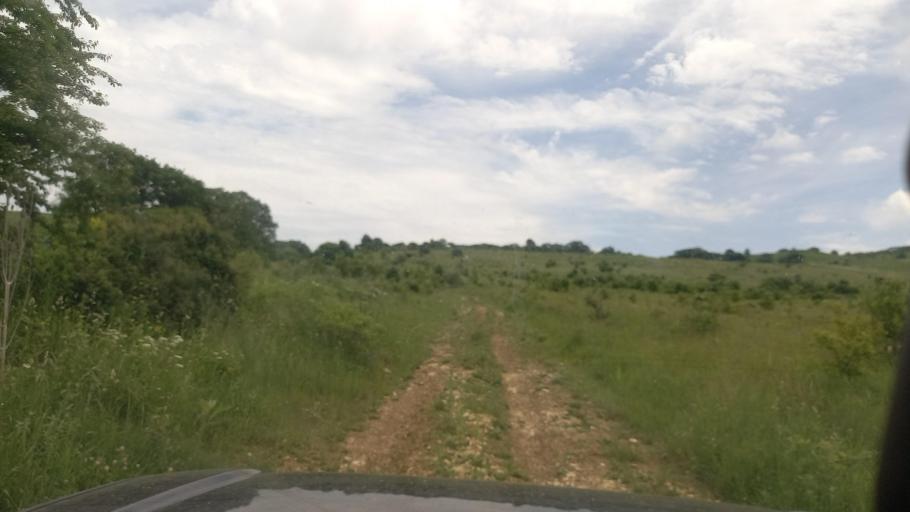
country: RU
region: Karachayevo-Cherkesiya
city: Pregradnaya
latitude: 44.0858
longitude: 41.2087
